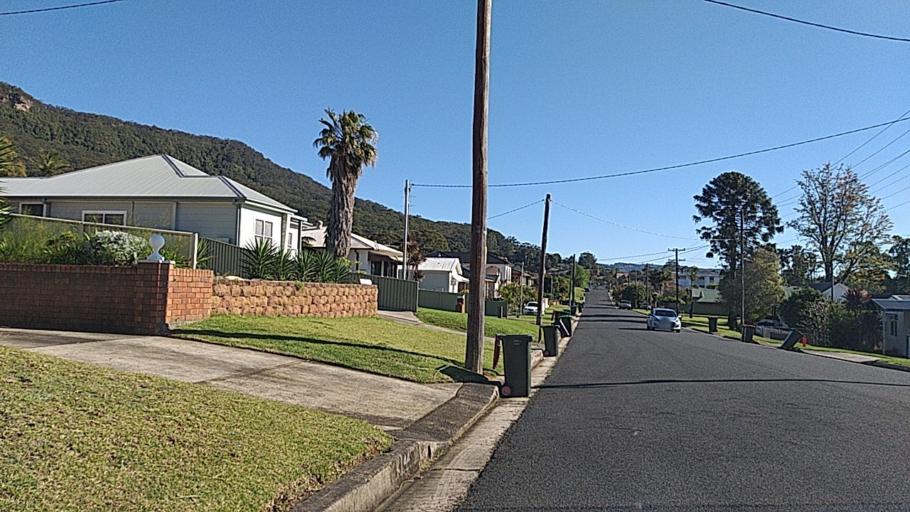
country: AU
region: New South Wales
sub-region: Wollongong
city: Corrimal
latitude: -34.3791
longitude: 150.8873
